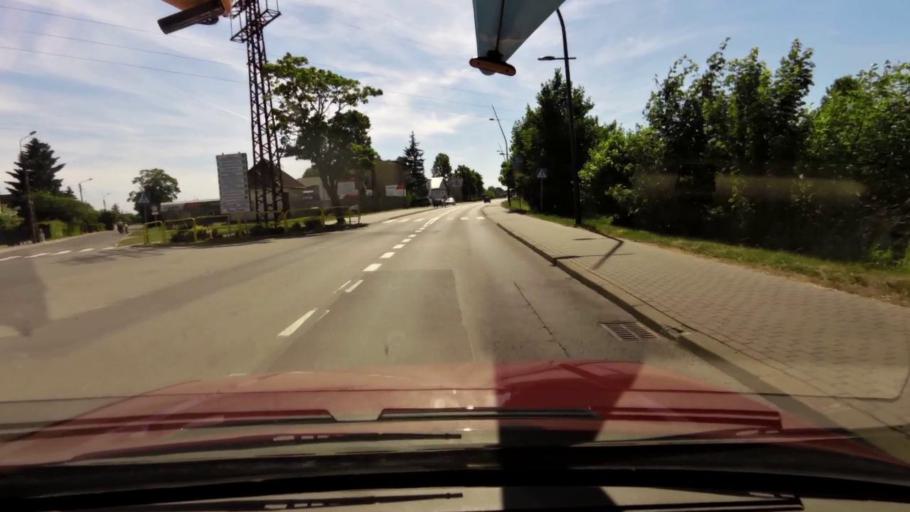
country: PL
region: Pomeranian Voivodeship
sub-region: Powiat slupski
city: Kobylnica
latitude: 54.4464
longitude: 17.0073
